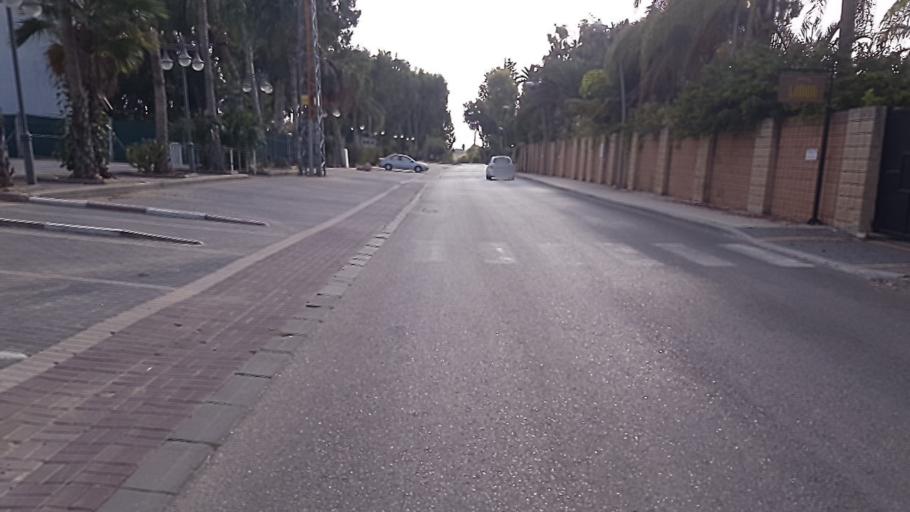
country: IL
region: Central District
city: Rosh Ha'Ayin
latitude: 32.0824
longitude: 34.9401
